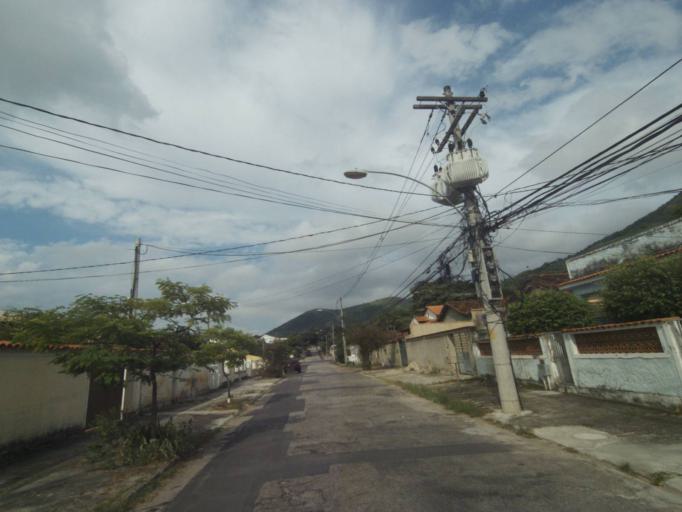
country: BR
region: Rio de Janeiro
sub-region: Nilopolis
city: Nilopolis
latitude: -22.8895
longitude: -43.3916
